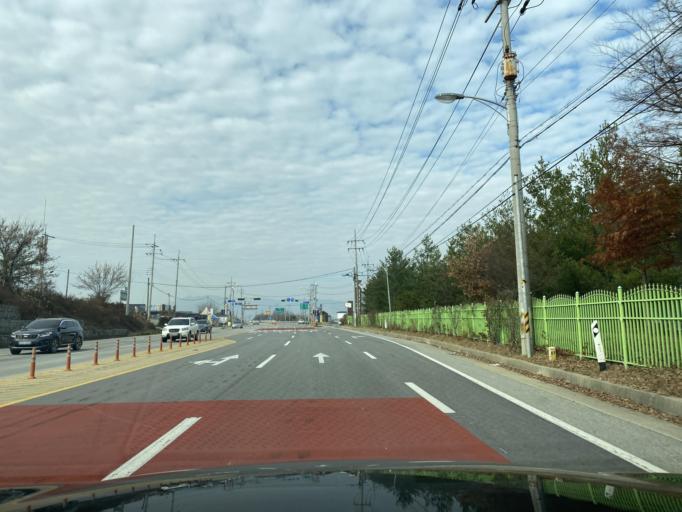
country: KR
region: Chungcheongnam-do
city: Yesan
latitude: 36.6894
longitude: 126.7520
